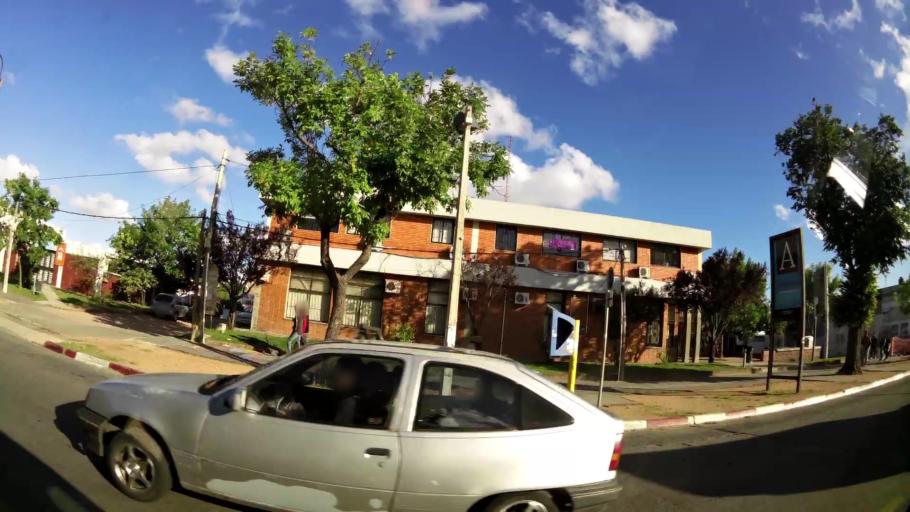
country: UY
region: Montevideo
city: Montevideo
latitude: -34.8661
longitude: -56.2361
